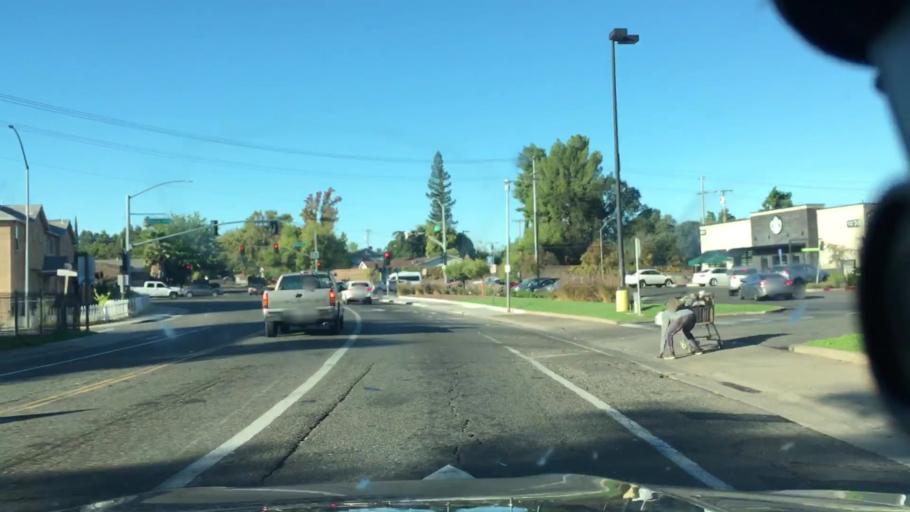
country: US
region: California
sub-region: Sacramento County
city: Foothill Farms
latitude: 38.6856
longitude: -121.3386
